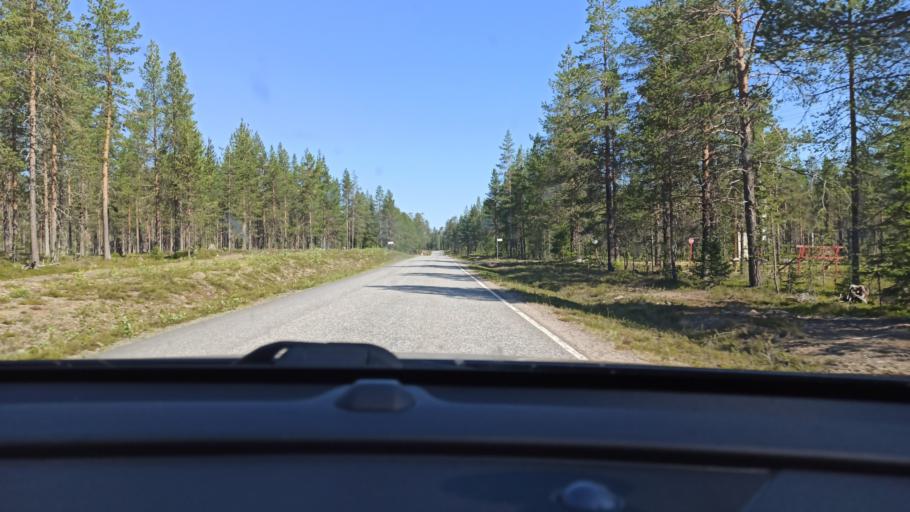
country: FI
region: Lapland
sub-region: Tunturi-Lappi
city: Kolari
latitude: 67.6555
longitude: 24.1640
